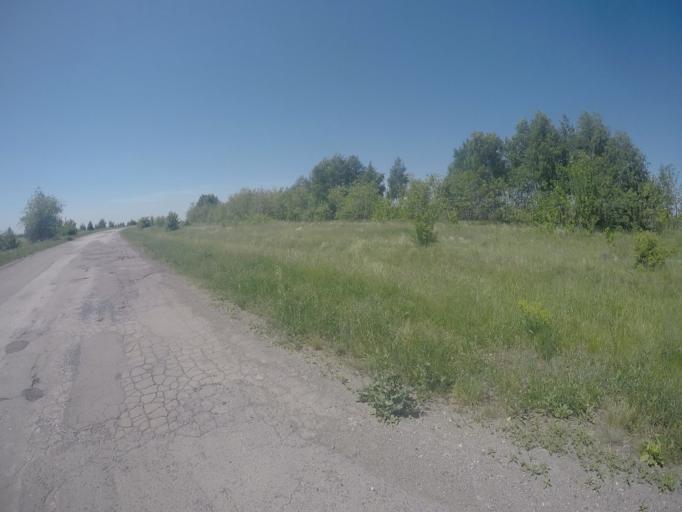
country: RU
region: Saratov
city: Krasnyy Oktyabr'
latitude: 51.2976
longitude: 45.5459
